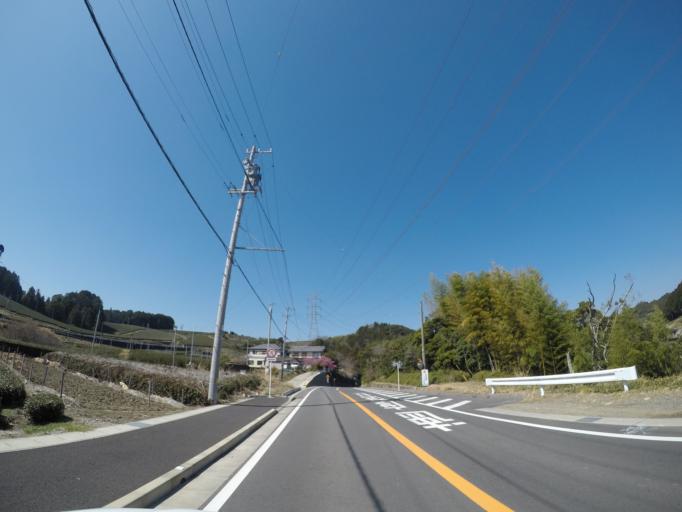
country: JP
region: Shizuoka
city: Kanaya
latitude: 34.7881
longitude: 138.1265
